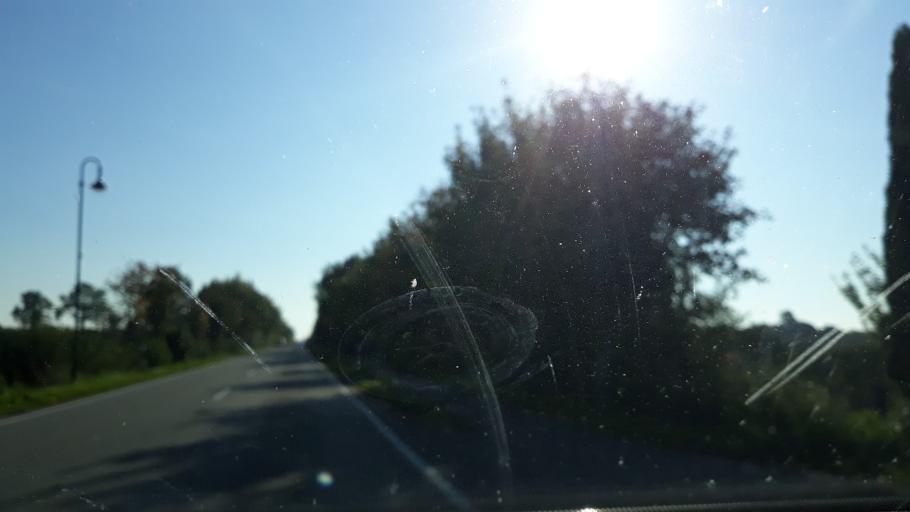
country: DE
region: Schleswig-Holstein
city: Boklund
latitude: 54.5983
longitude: 9.5861
